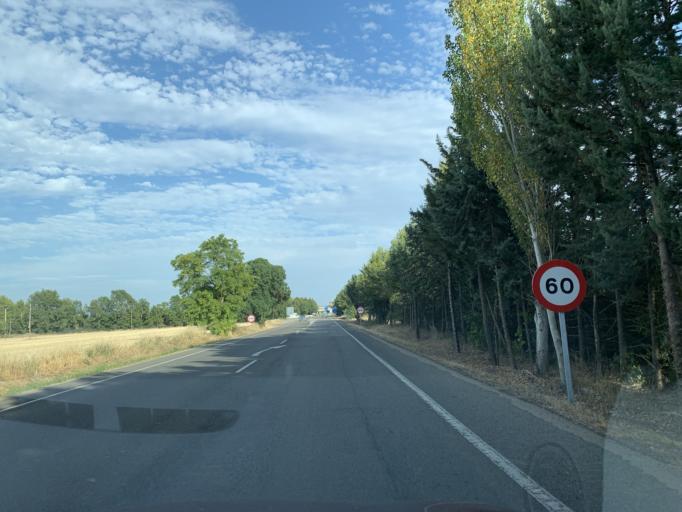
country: ES
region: Aragon
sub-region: Provincia de Huesca
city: Chimillas
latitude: 42.1517
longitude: -0.4331
